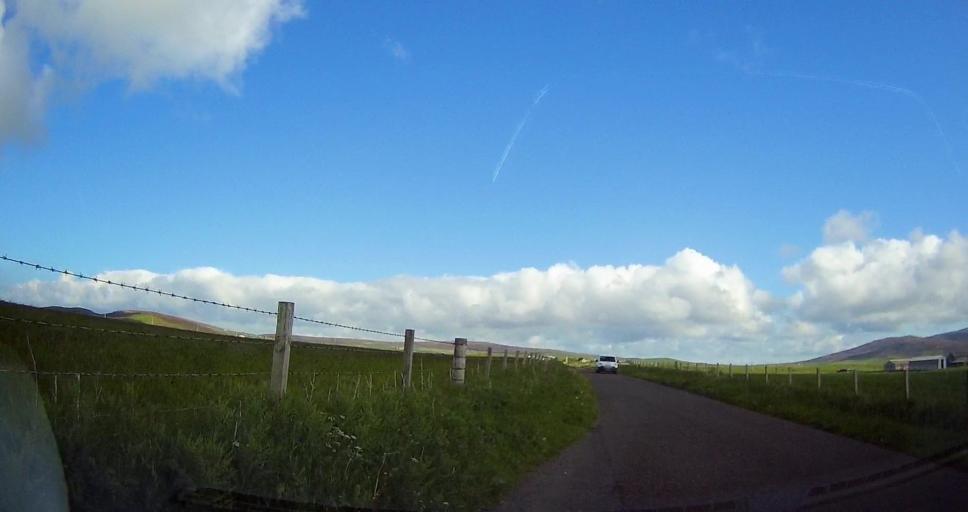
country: GB
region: Scotland
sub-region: Orkney Islands
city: Stromness
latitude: 58.9995
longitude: -3.1706
